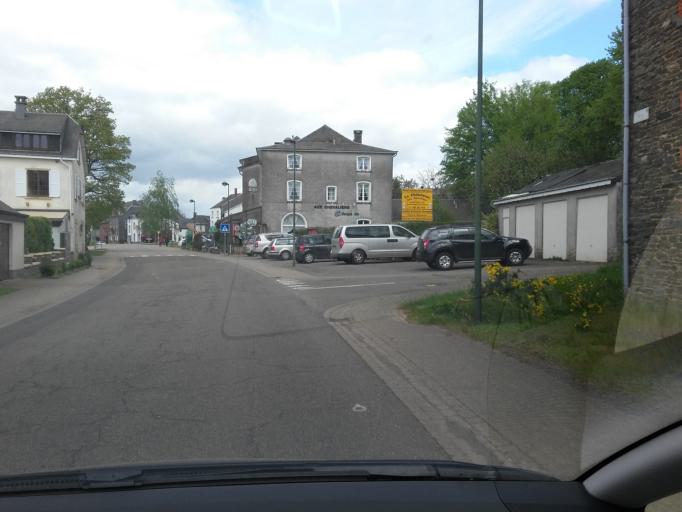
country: BE
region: Wallonia
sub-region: Province du Luxembourg
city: Herbeumont
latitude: 49.7799
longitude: 5.2390
